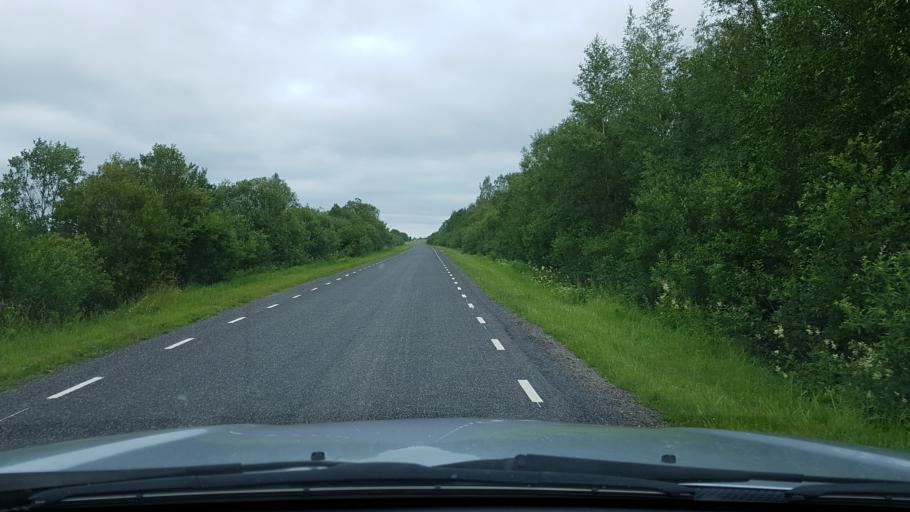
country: EE
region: Ida-Virumaa
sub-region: Narva linn
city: Narva
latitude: 59.3752
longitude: 28.1135
